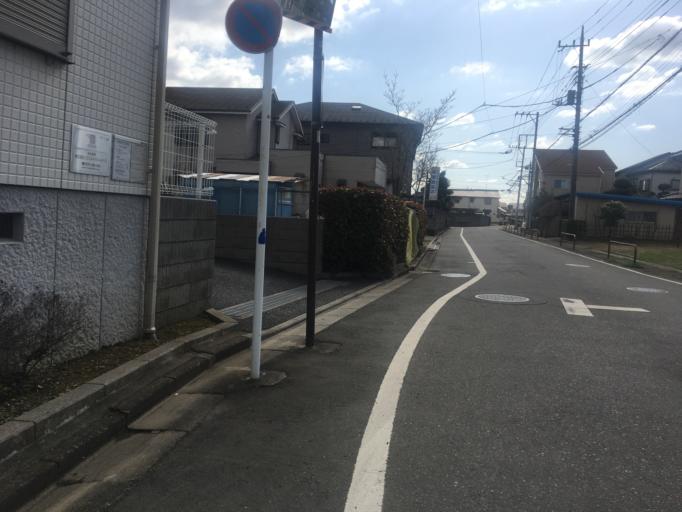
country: JP
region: Saitama
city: Shiki
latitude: 35.8703
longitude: 139.5937
